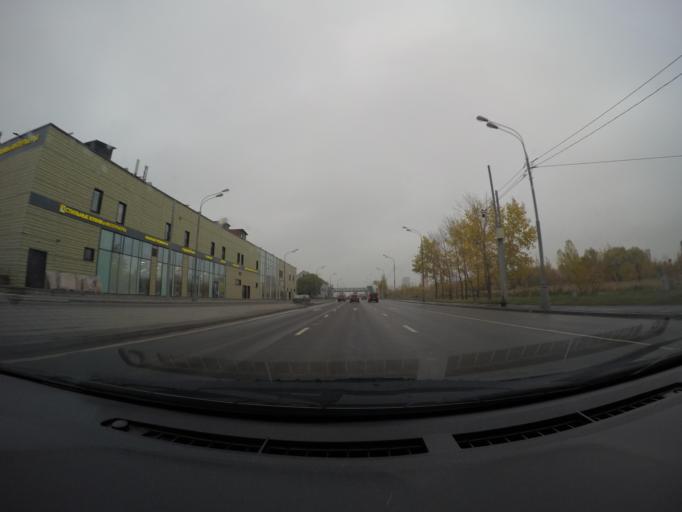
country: RU
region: Moskovskaya
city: Shcherbinka
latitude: 55.5150
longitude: 37.5767
